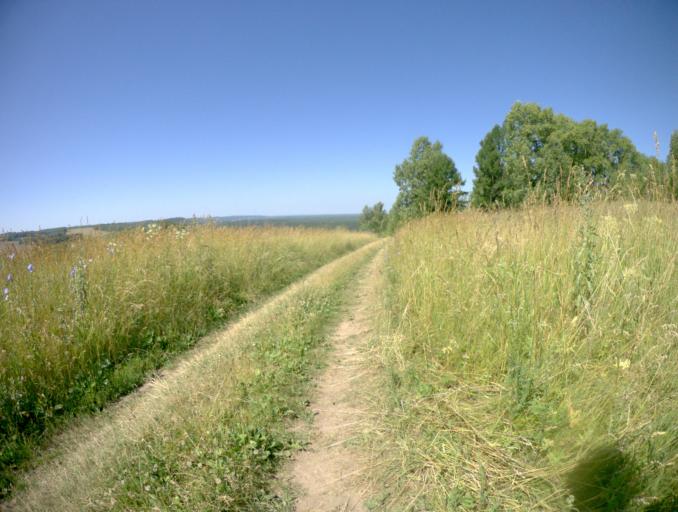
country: RU
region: Nizjnij Novgorod
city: Reshetikha
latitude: 56.1366
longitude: 43.2923
